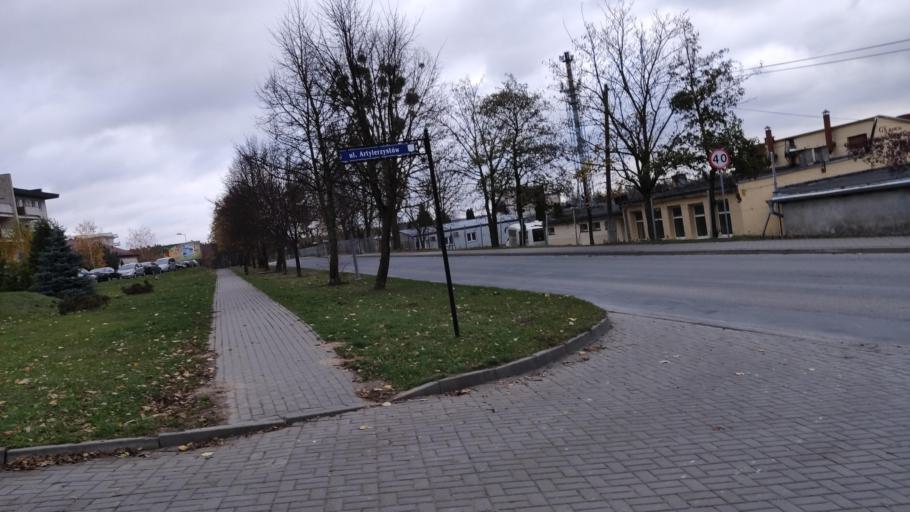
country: PL
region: Kujawsko-Pomorskie
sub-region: Powiat zninski
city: Barcin
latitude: 52.8526
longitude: 17.9479
